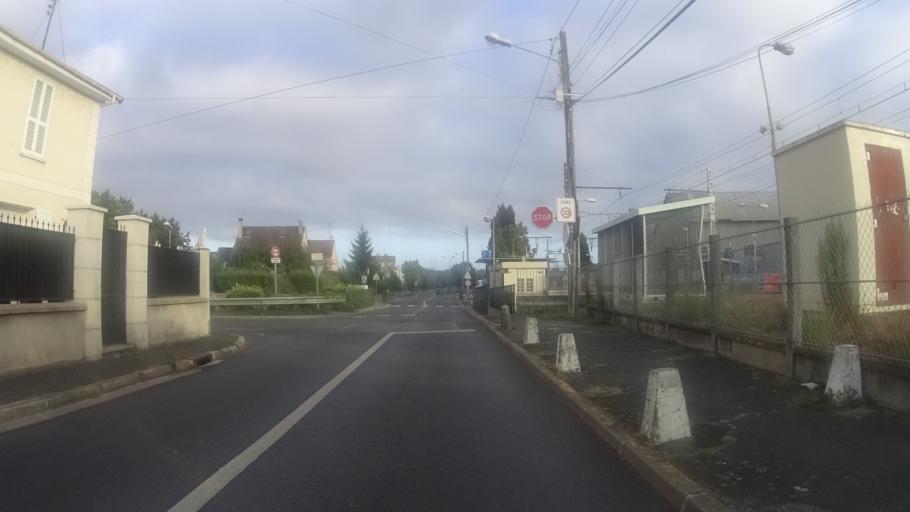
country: FR
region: Ile-de-France
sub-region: Departement de l'Essonne
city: Villabe
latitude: 48.5923
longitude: 2.4621
